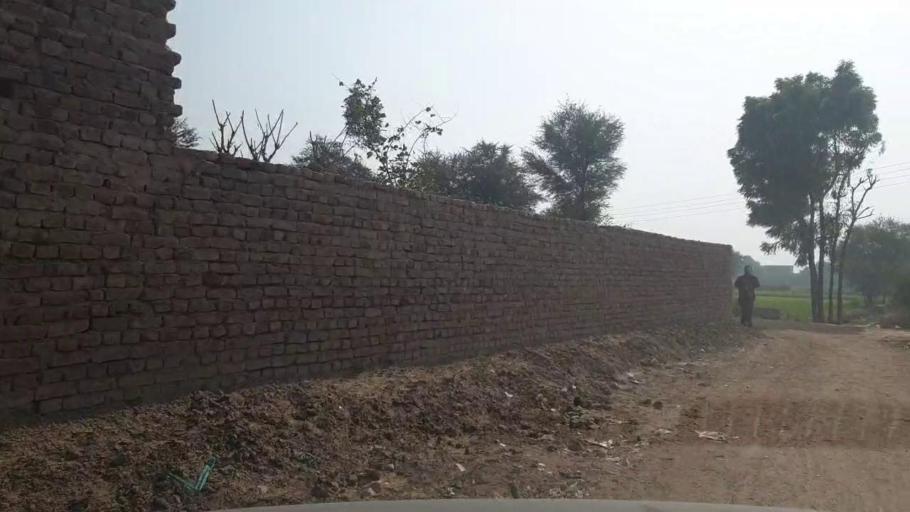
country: PK
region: Sindh
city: Hala
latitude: 25.7618
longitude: 68.4336
